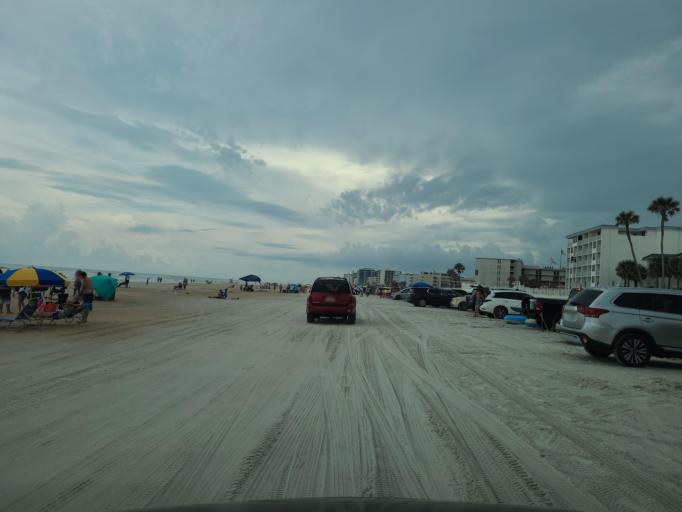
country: US
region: Florida
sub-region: Volusia County
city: Daytona Beach
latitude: 29.2150
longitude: -81.0009
